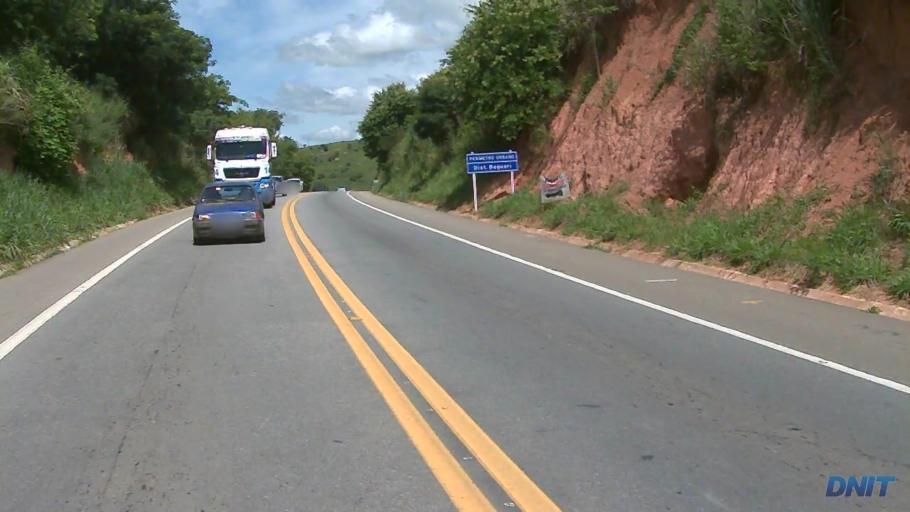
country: BR
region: Minas Gerais
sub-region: Governador Valadares
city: Governador Valadares
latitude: -18.9541
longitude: -42.0729
